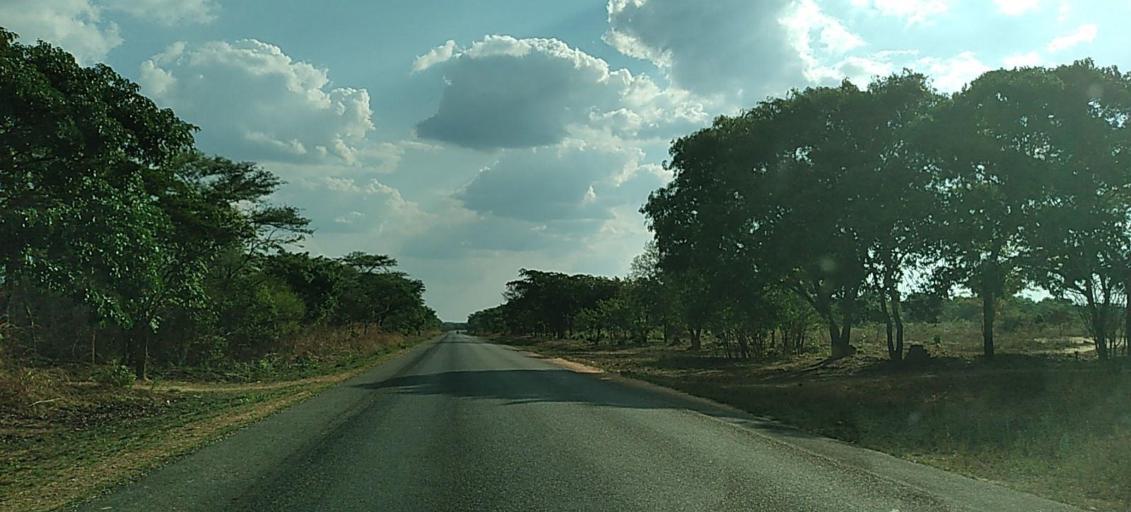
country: ZM
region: Copperbelt
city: Luanshya
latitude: -13.3805
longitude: 28.3936
